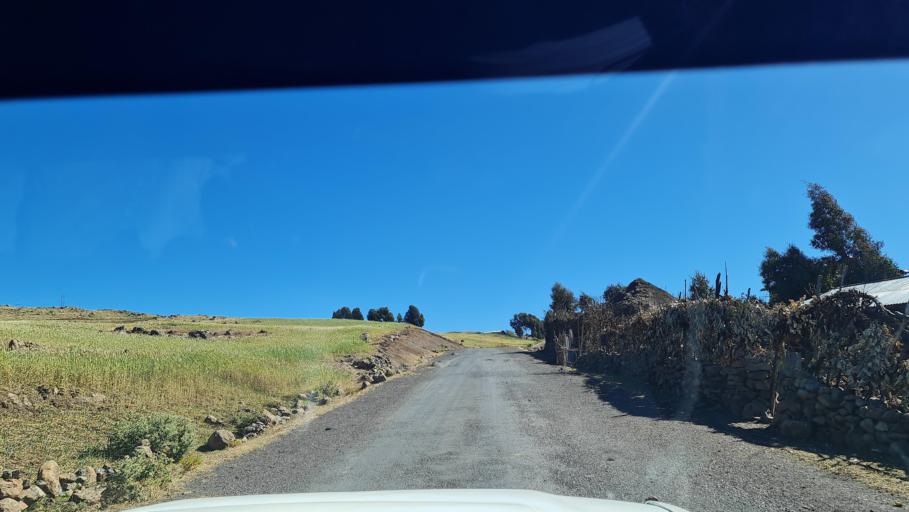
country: ET
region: Amhara
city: Debark'
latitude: 13.1335
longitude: 38.1710
